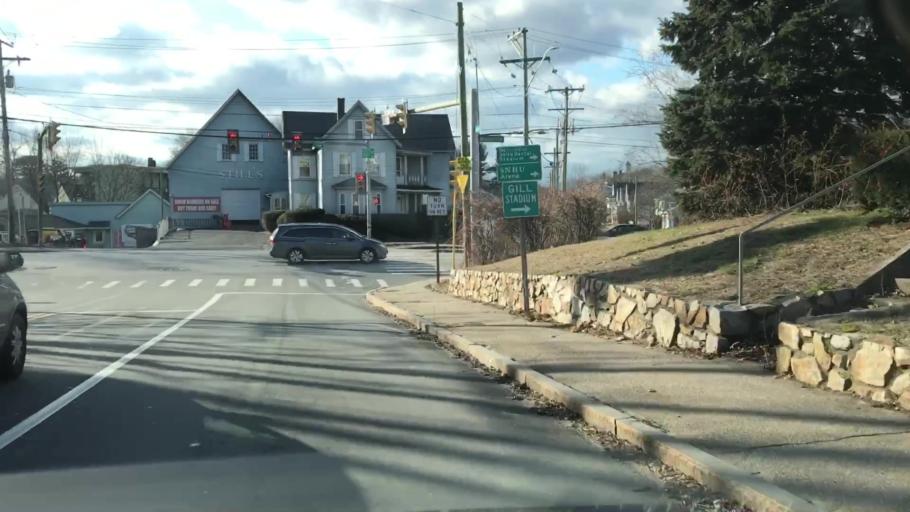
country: US
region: New Hampshire
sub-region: Hillsborough County
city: Manchester
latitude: 42.9798
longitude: -71.4308
